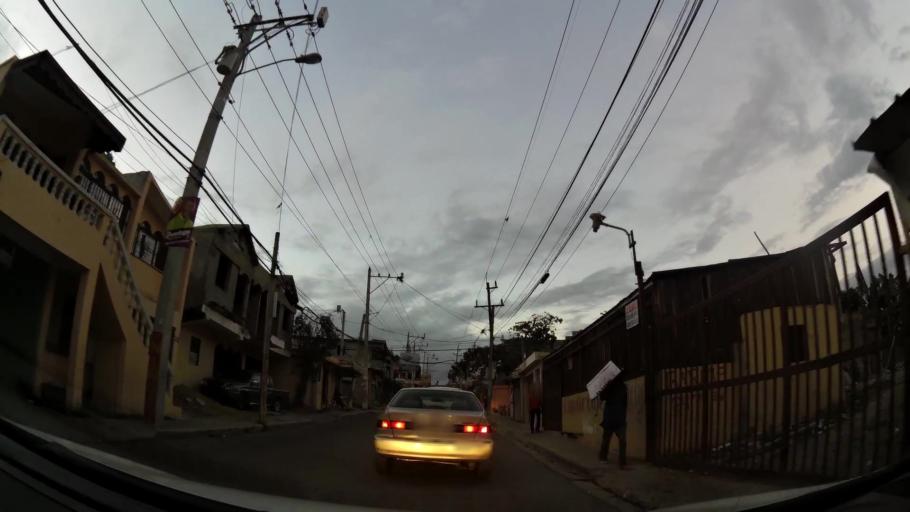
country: DO
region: Santo Domingo
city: Santo Domingo Oeste
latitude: 18.5217
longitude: -70.0339
